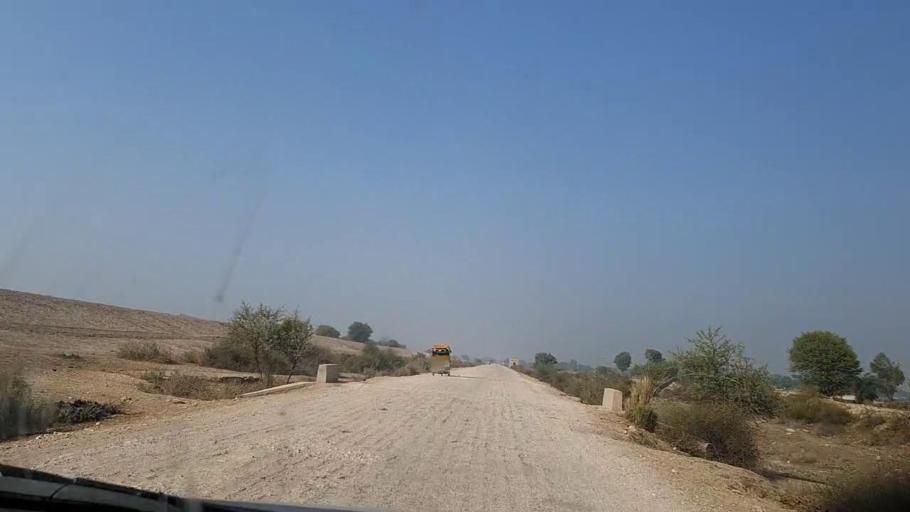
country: PK
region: Sindh
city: Moro
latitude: 26.7216
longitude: 67.9227
